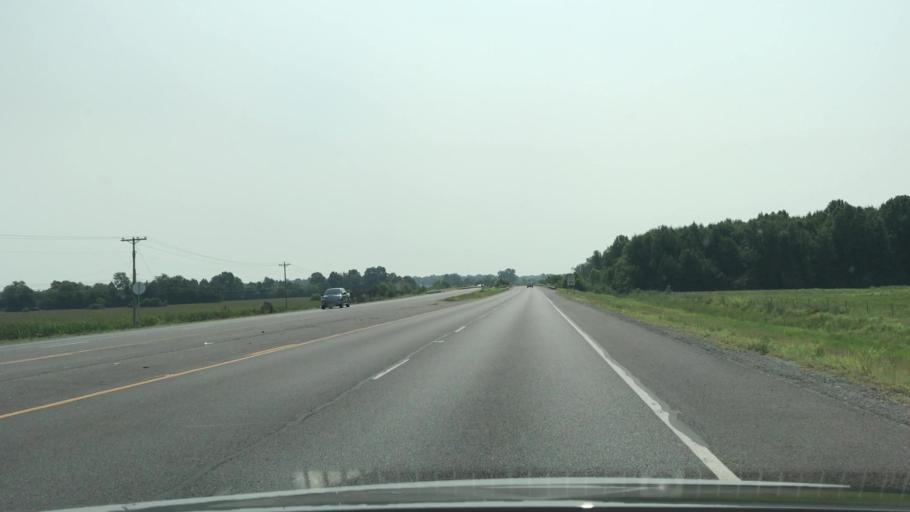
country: US
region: Kentucky
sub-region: Graves County
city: Mayfield
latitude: 36.7146
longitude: -88.6192
